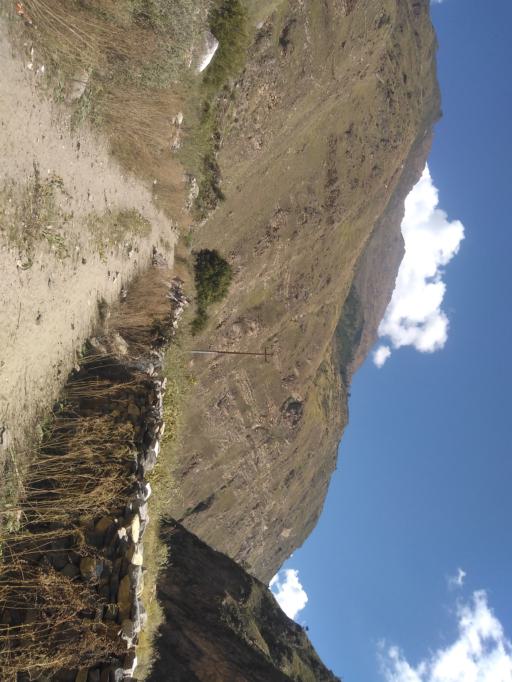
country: NP
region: Western Region
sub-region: Dhawalagiri Zone
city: Jomsom
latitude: 28.9376
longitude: 82.9542
